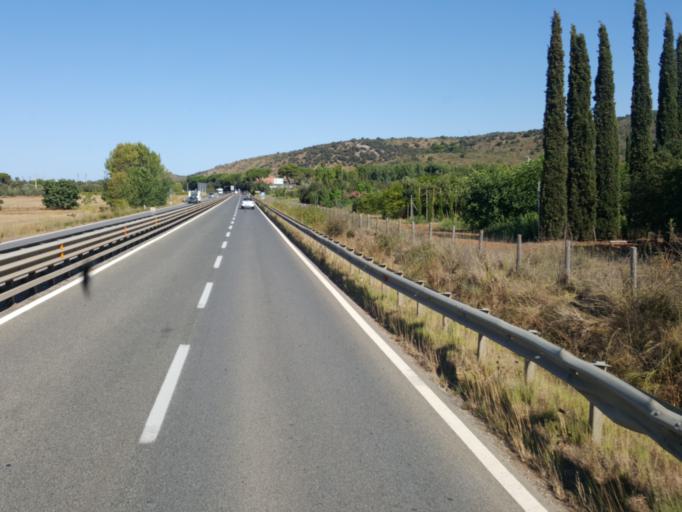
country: IT
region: Tuscany
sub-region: Provincia di Grosseto
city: Orbetello Scalo
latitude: 42.4331
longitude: 11.2827
